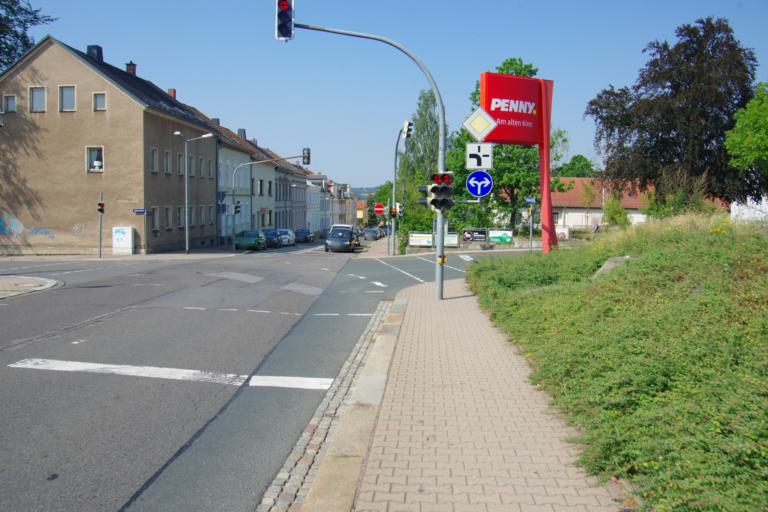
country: DE
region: Saxony
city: Frankenberg
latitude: 50.9102
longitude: 13.0394
